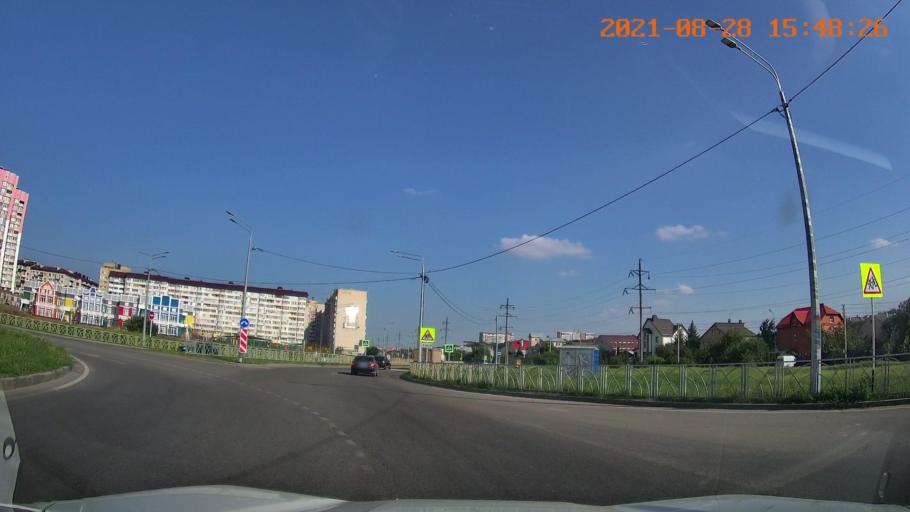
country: RU
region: Stavropol'skiy
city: Tatarka
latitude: 44.9972
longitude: 41.9094
